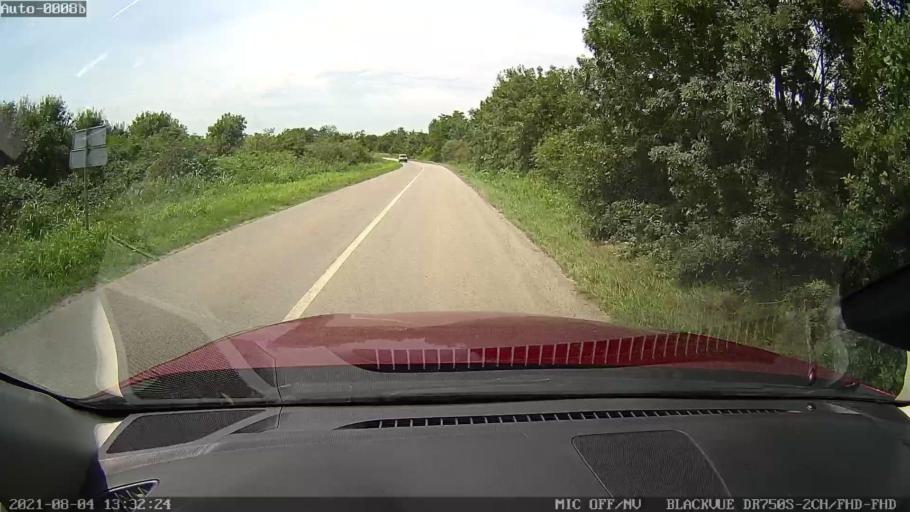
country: HR
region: Osjecko-Baranjska
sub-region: Grad Osijek
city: Bilje
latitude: 45.6080
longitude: 18.7605
